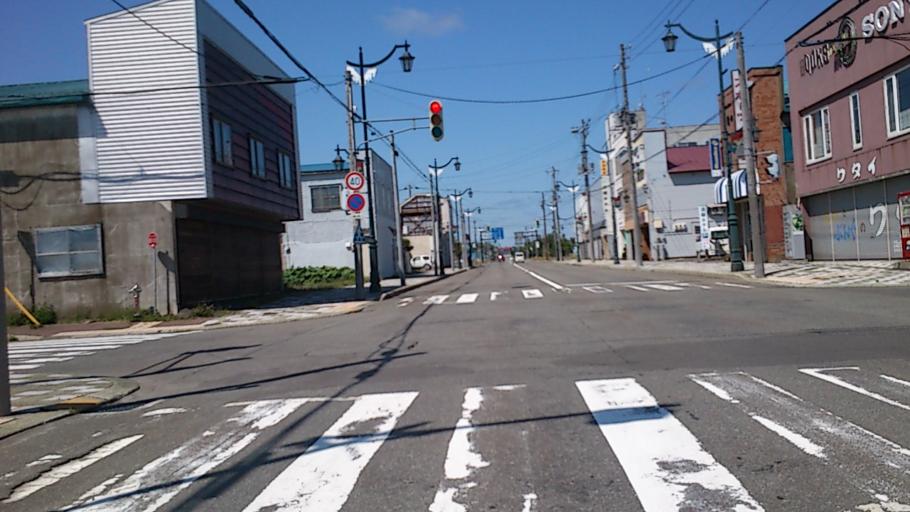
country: JP
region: Hokkaido
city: Makubetsu
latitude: 45.1249
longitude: 142.3634
